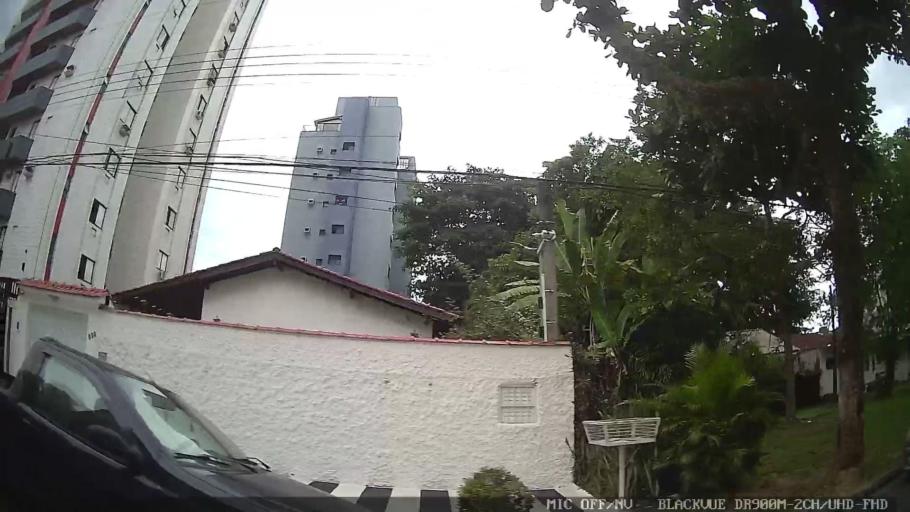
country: BR
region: Sao Paulo
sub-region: Guaruja
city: Guaruja
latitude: -24.0105
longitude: -46.2748
